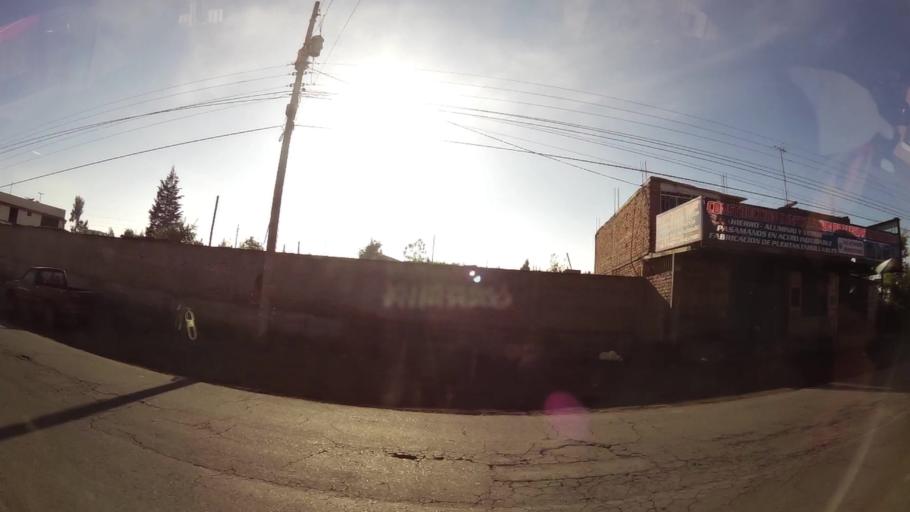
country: EC
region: Chimborazo
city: Riobamba
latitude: -1.6469
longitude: -78.6417
